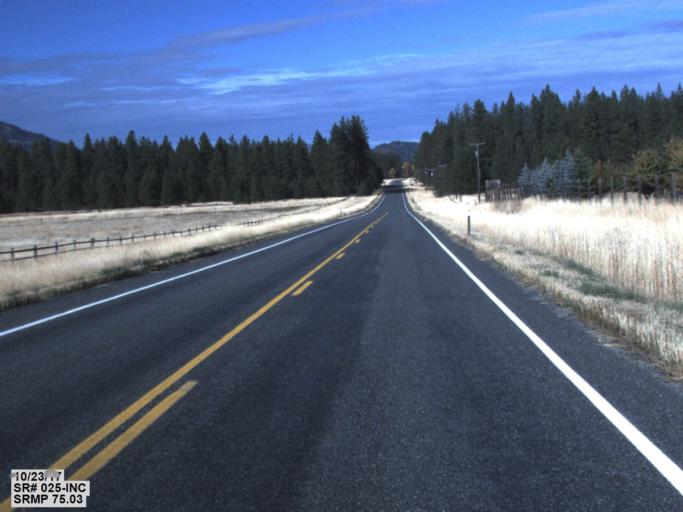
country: US
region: Washington
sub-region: Stevens County
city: Kettle Falls
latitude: 48.5411
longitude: -118.1310
